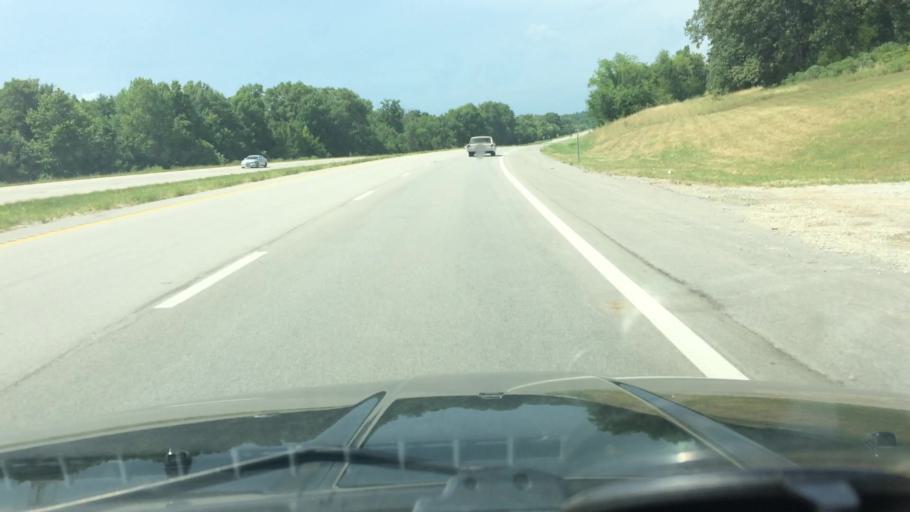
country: US
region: Missouri
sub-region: Henry County
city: Clinton
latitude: 38.2154
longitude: -93.7601
